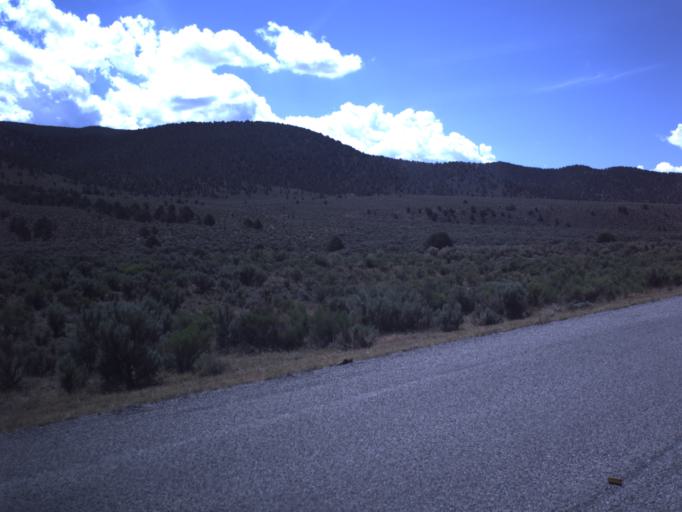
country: US
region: Utah
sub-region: Piute County
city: Junction
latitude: 38.0622
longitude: -112.3483
